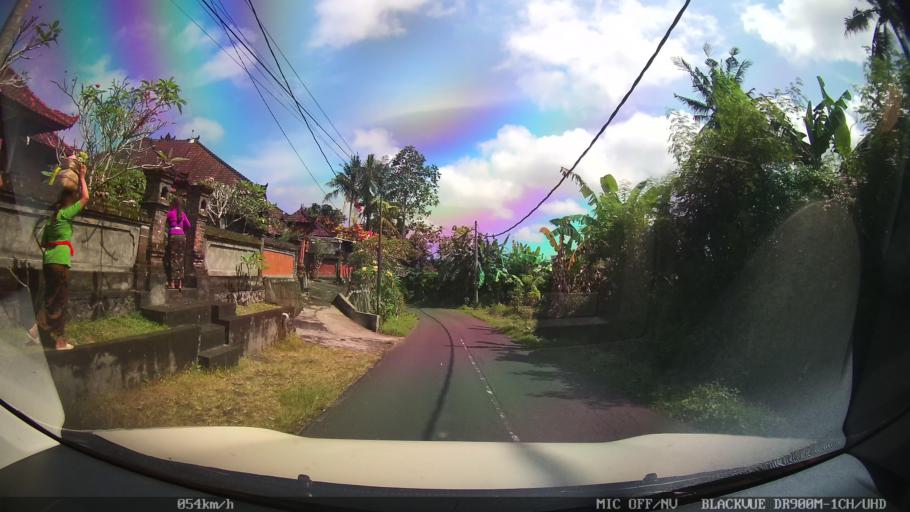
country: ID
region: Bali
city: Banjar Kelodan
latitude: -8.5239
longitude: 115.3290
